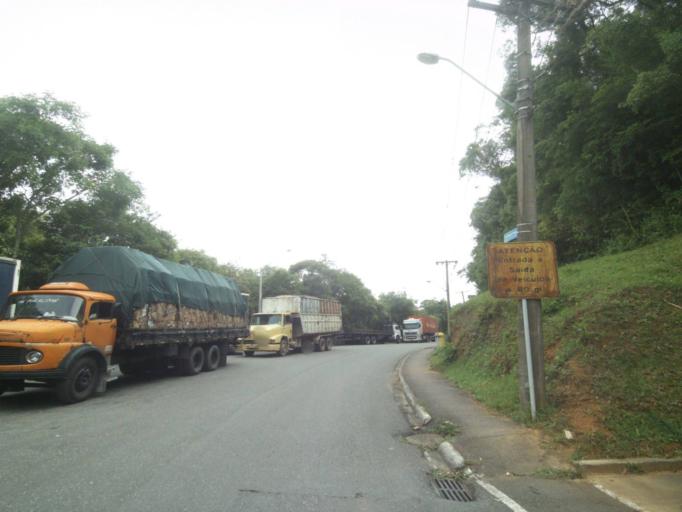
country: BR
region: Parana
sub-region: Curitiba
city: Curitiba
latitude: -25.4083
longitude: -49.3065
